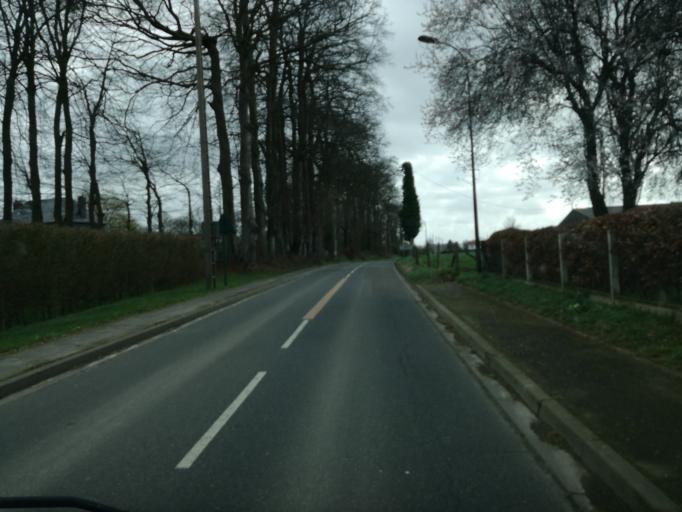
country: FR
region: Haute-Normandie
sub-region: Departement de la Seine-Maritime
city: Yebleron
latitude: 49.6647
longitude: 0.5049
